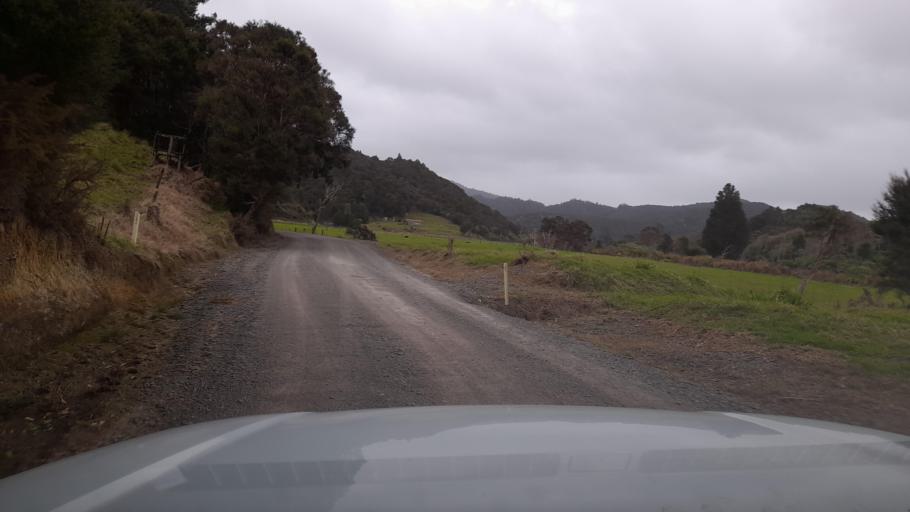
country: NZ
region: Northland
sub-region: Far North District
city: Paihia
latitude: -35.3424
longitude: 174.2298
